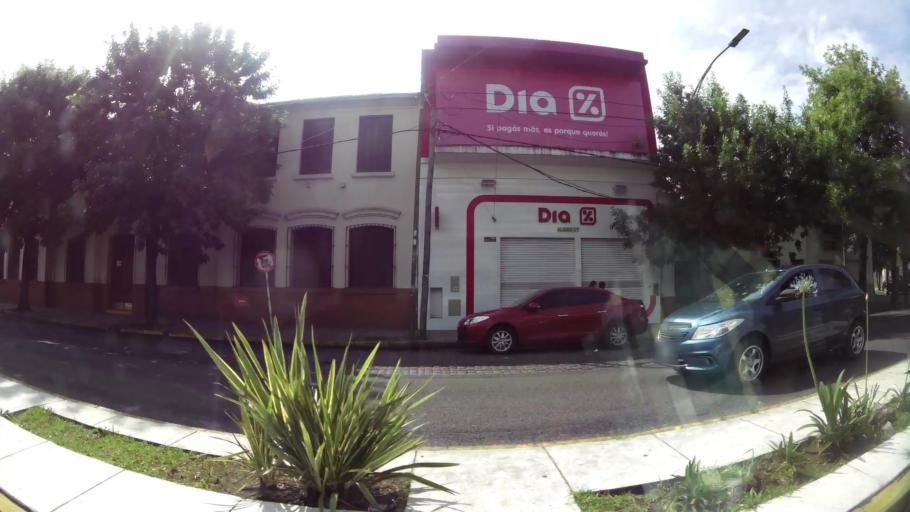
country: AR
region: Buenos Aires F.D.
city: Villa Lugano
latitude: -34.6680
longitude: -58.5068
